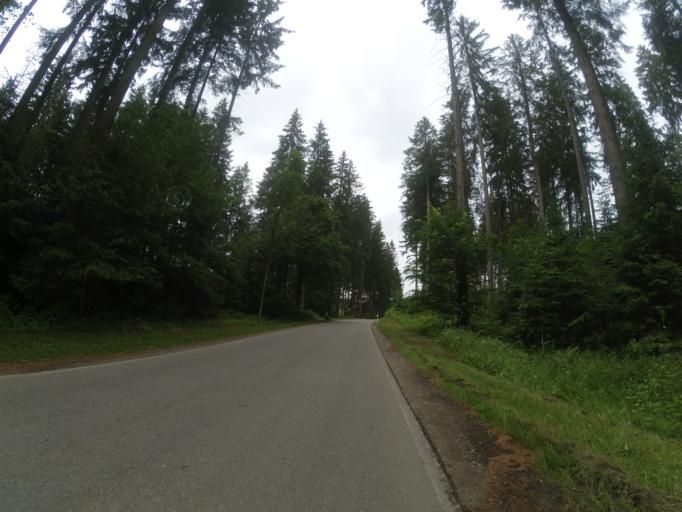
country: DE
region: Baden-Wuerttemberg
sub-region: Tuebingen Region
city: Isny im Allgau
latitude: 47.7349
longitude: 10.0395
